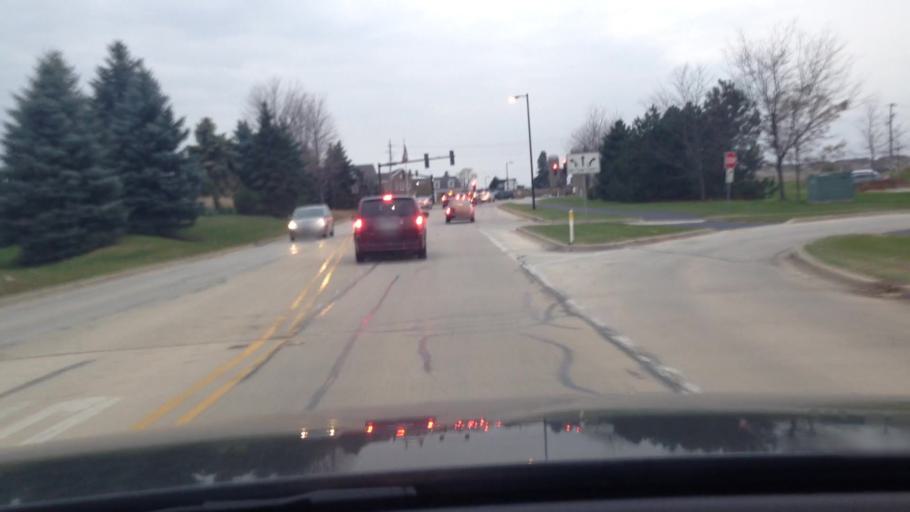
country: US
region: Illinois
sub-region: McHenry County
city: Huntley
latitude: 42.1830
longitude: -88.4206
